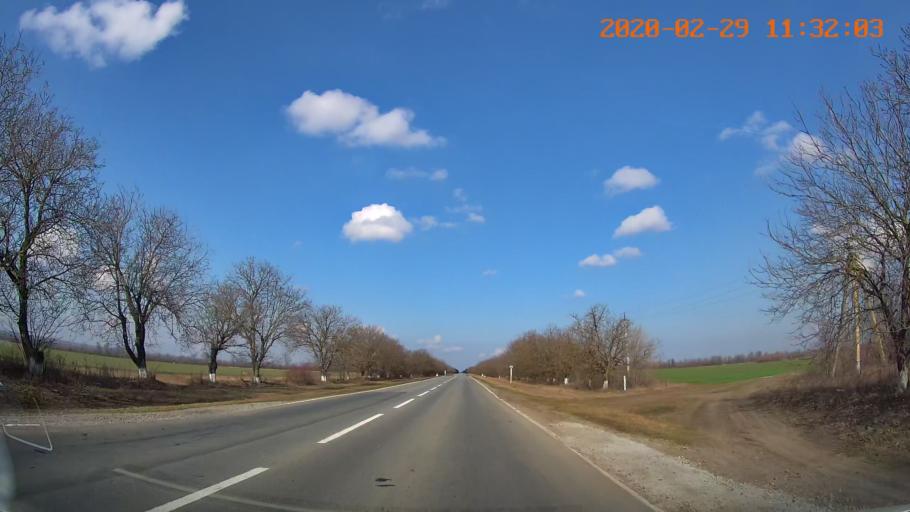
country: MD
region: Rezina
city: Saharna
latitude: 47.5323
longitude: 29.0985
